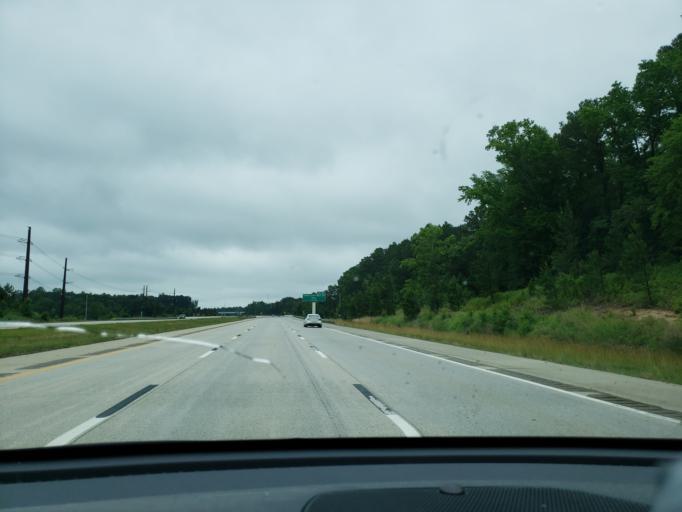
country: US
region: North Carolina
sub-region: Wake County
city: Green Level
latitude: 35.7743
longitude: -78.8854
